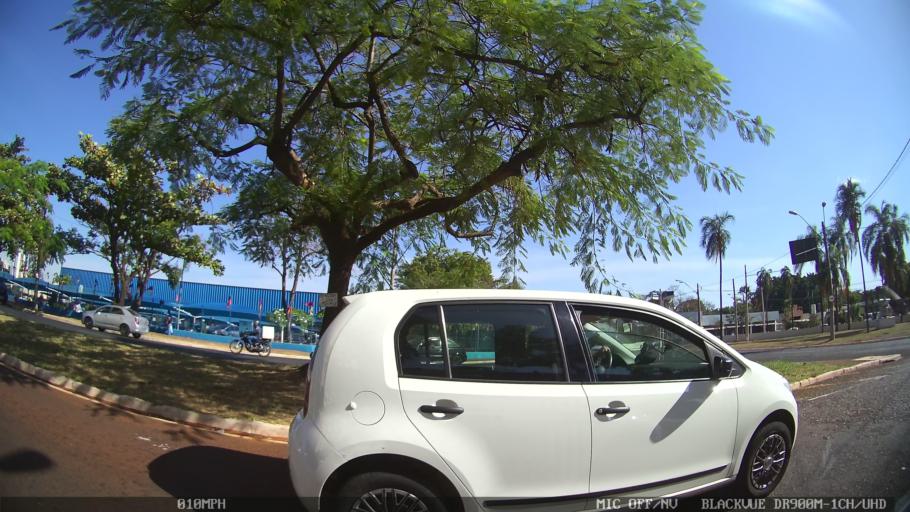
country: BR
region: Sao Paulo
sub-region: Ribeirao Preto
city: Ribeirao Preto
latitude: -21.1744
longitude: -47.7942
